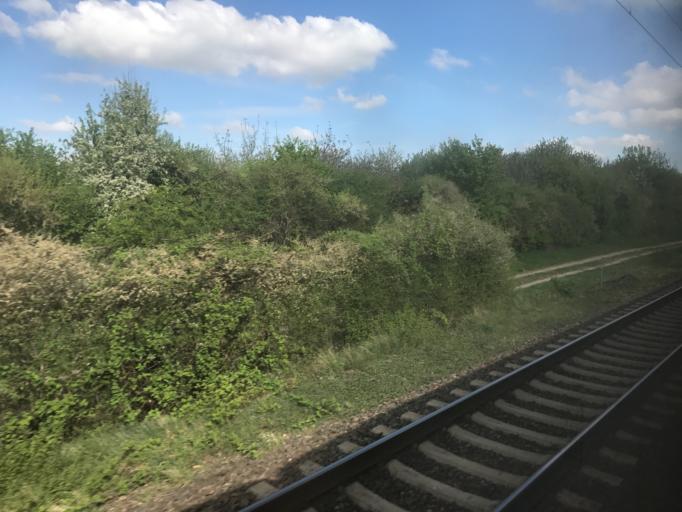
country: DE
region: Rheinland-Pfalz
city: Mettenheim
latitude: 49.7362
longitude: 8.3330
